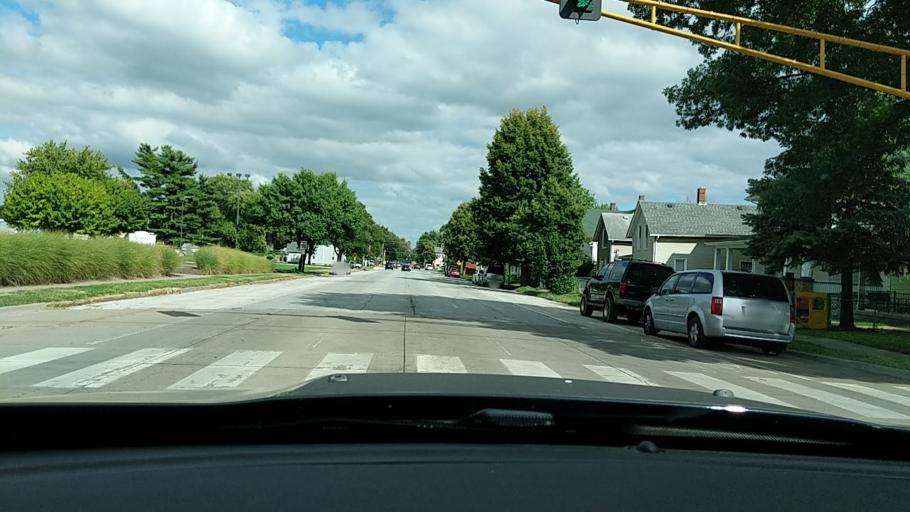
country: US
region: Iowa
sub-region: Scott County
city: Davenport
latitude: 41.5223
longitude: -90.6053
